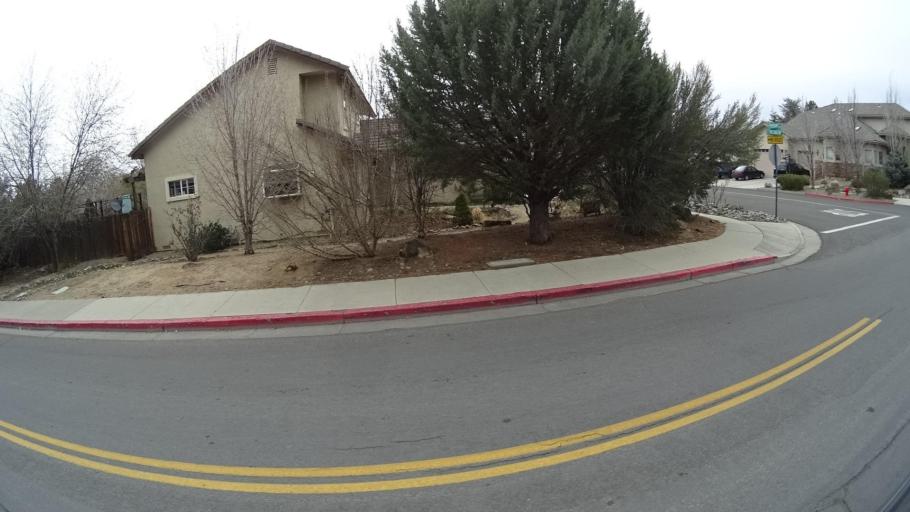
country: US
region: Nevada
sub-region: Washoe County
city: Reno
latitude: 39.5449
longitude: -119.8265
